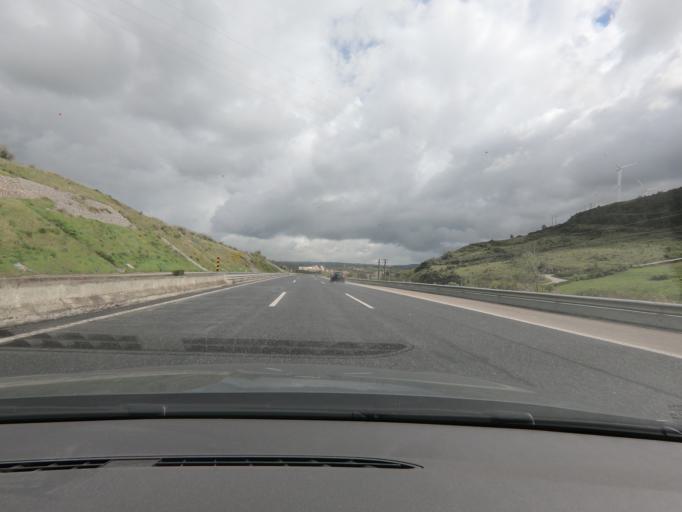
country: PT
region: Lisbon
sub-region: Loures
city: Bucelas
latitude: 38.8878
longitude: -9.1271
